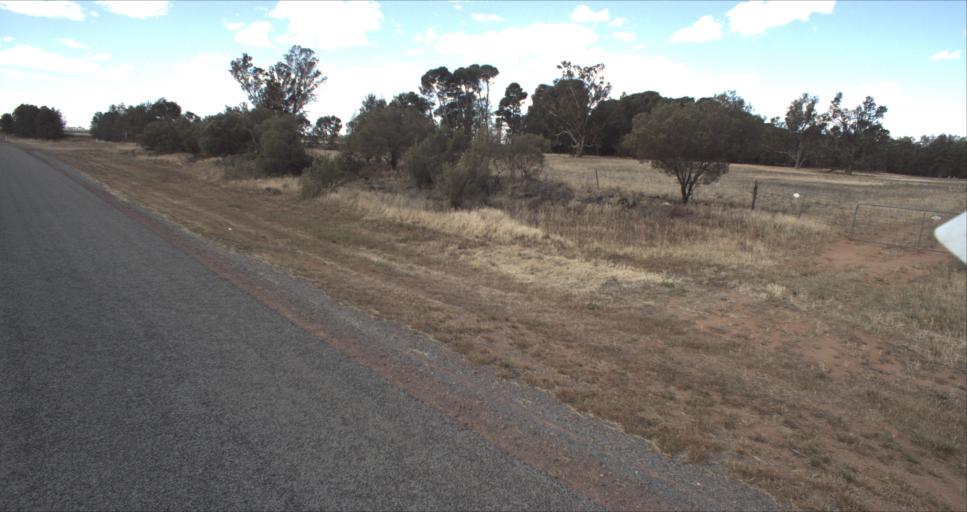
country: AU
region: New South Wales
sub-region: Leeton
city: Leeton
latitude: -34.4835
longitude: 146.2486
